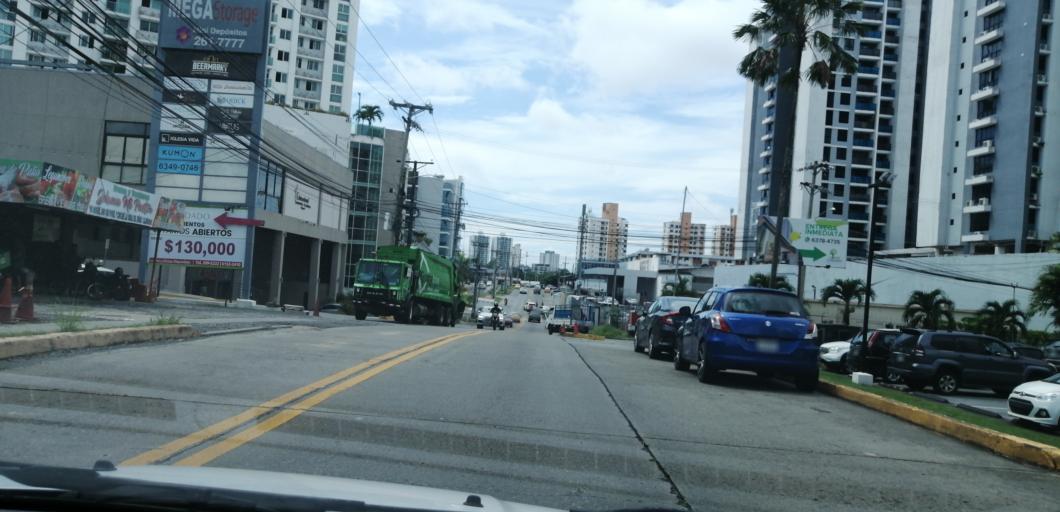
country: PA
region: Panama
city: Panama
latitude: 9.0270
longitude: -79.5243
